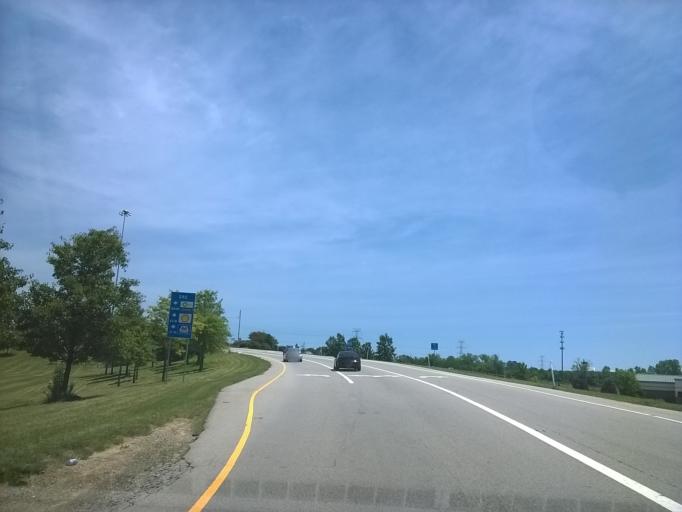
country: US
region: Ohio
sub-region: Butler County
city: Beckett Ridge
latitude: 39.3205
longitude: -84.4243
